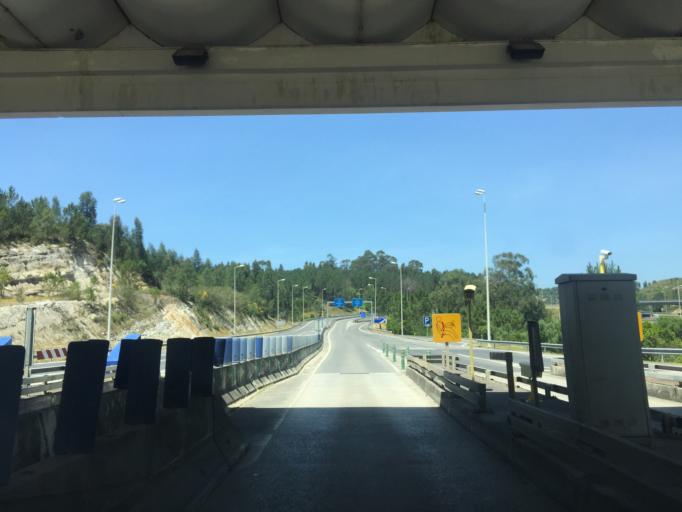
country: PT
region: Lisbon
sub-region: Mafra
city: Venda do Pinheiro
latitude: 38.9040
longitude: -9.2059
